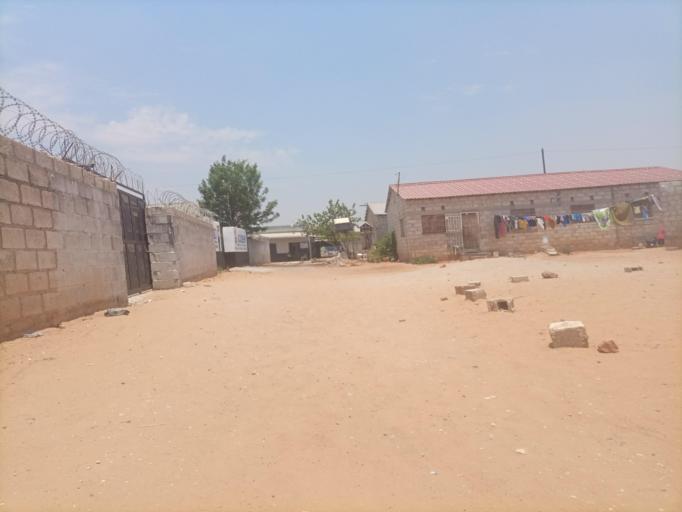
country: ZM
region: Lusaka
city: Lusaka
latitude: -15.4080
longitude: 28.3718
